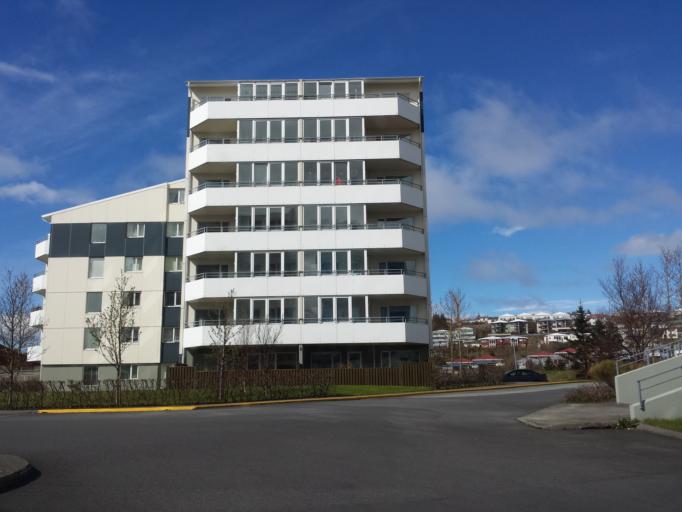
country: IS
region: Capital Region
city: Kopavogur
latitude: 64.1047
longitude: -21.8805
